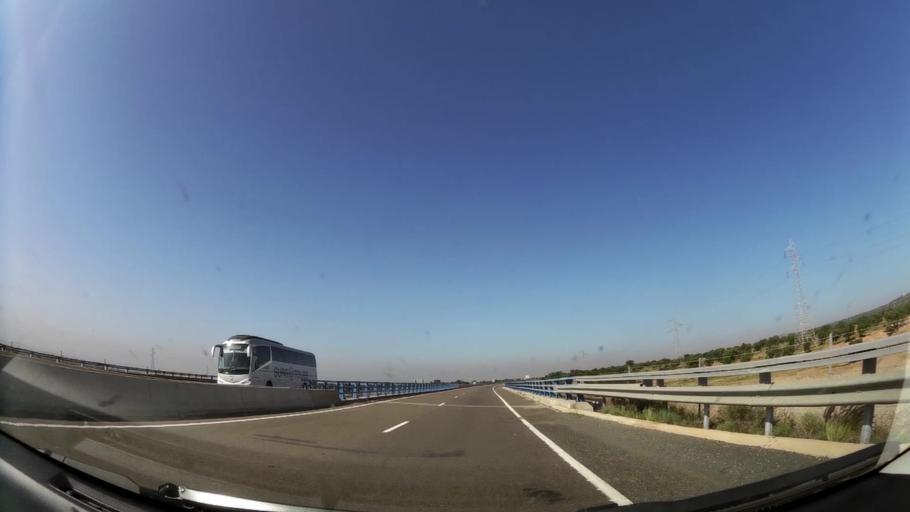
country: MA
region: Souss-Massa-Draa
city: Oulad Teima
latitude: 30.4281
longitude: -9.3770
